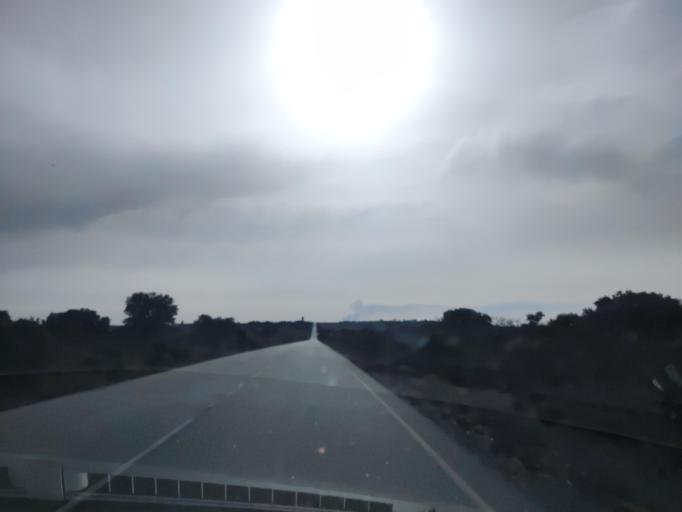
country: ES
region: Castille and Leon
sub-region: Provincia de Salamanca
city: Aldea del Obispo
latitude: 40.6518
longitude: -6.7994
